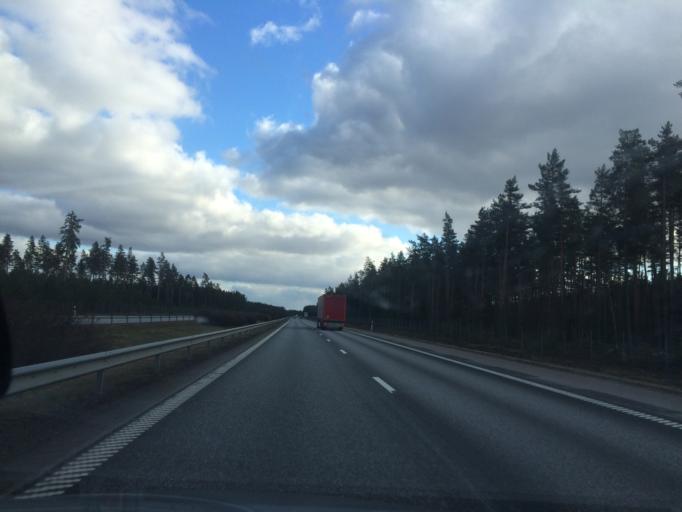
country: SE
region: Joenkoeping
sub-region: Vaggeryds Kommun
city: Skillingaryd
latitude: 57.3740
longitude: 14.1015
